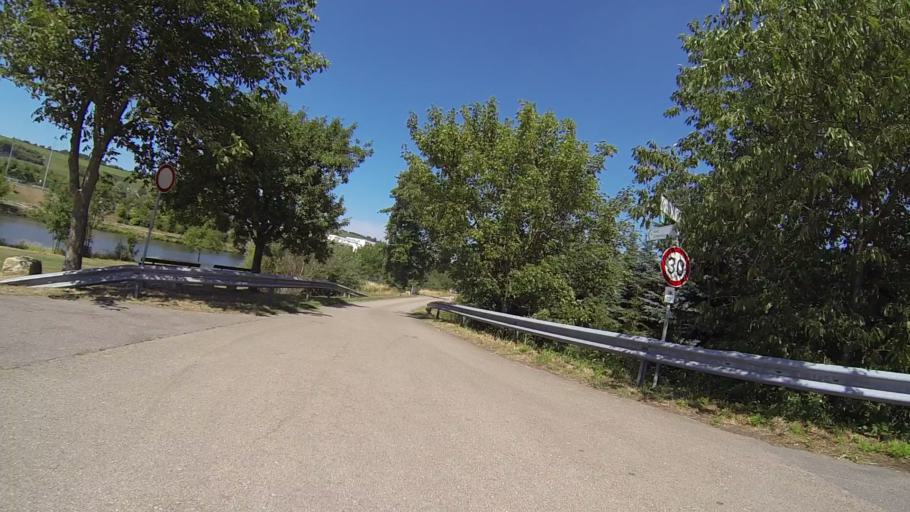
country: LU
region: Grevenmacher
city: Wasserbillig
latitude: 49.7058
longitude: 6.4929
